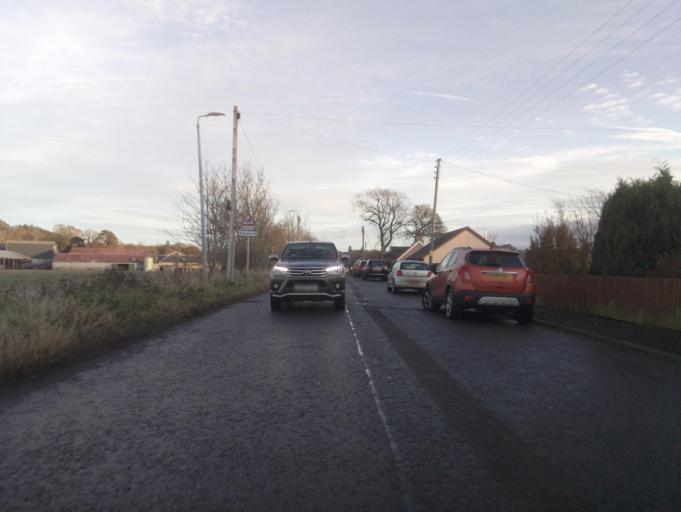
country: GB
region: Scotland
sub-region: Angus
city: Forfar
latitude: 56.5863
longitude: -2.8982
